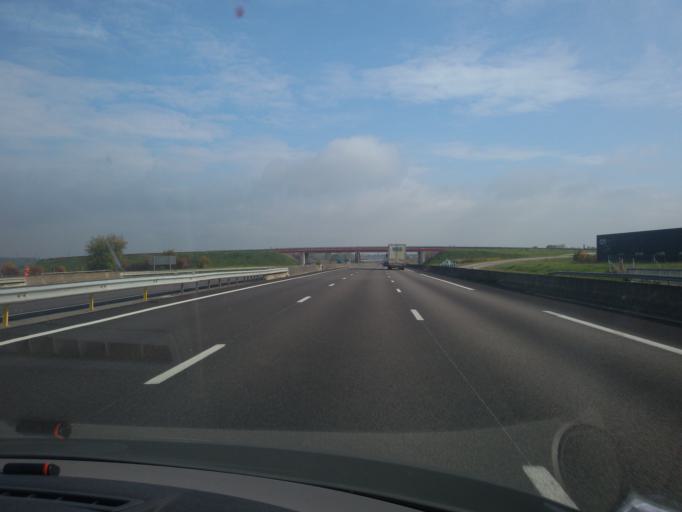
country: FR
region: Haute-Normandie
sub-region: Departement de l'Eure
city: Bourg-Achard
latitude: 49.3641
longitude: 0.8280
